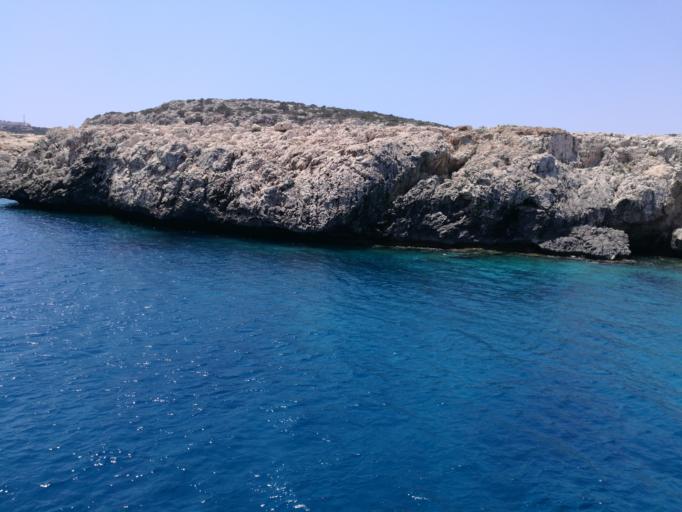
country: CY
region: Ammochostos
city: Protaras
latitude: 34.9749
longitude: 34.0772
